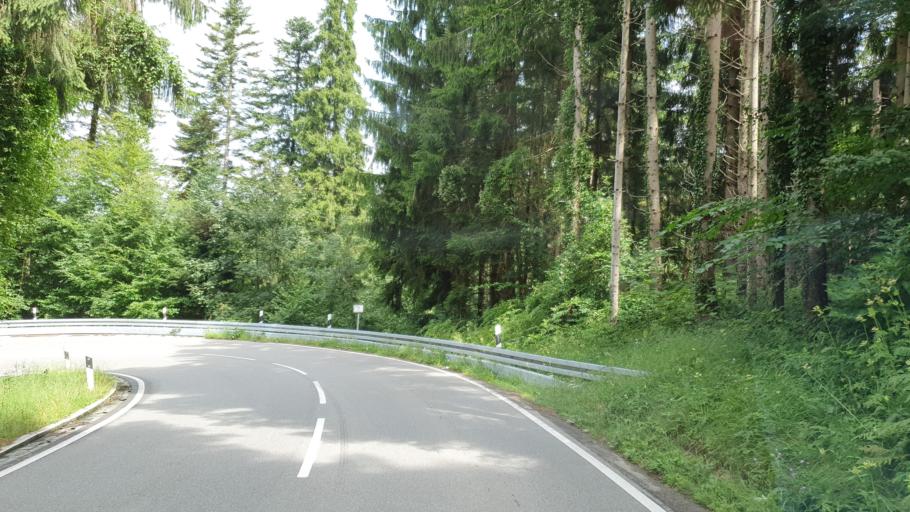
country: AT
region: Vorarlberg
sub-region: Politischer Bezirk Bregenz
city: Moggers
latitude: 47.5945
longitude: 9.8153
